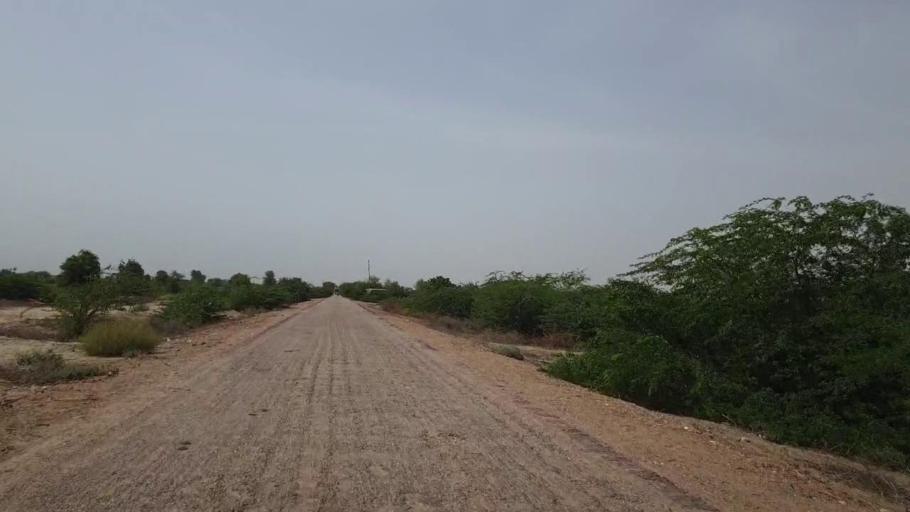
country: PK
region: Sindh
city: Bandhi
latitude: 26.5499
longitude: 68.3843
